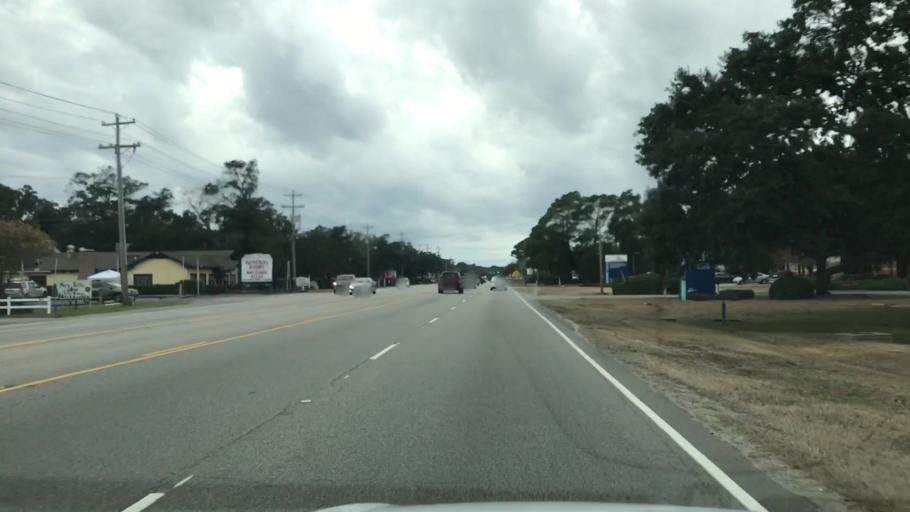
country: US
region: South Carolina
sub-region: Georgetown County
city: Murrells Inlet
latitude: 33.4332
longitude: -79.1390
